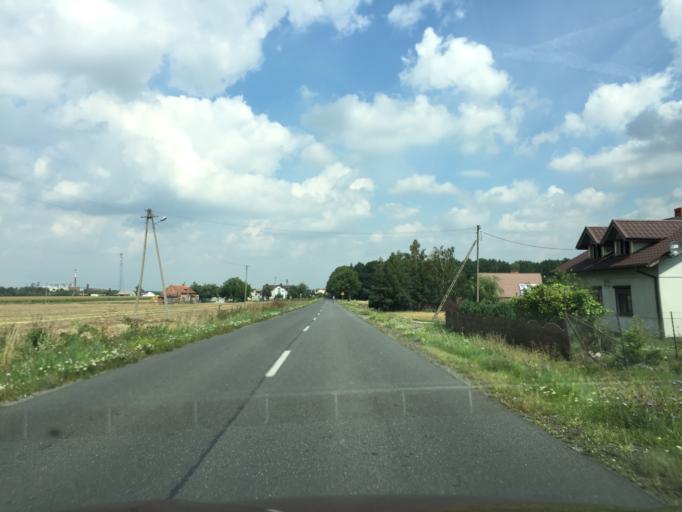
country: PL
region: Greater Poland Voivodeship
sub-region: Powiat kaliski
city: Stawiszyn
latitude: 51.9381
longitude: 18.1492
